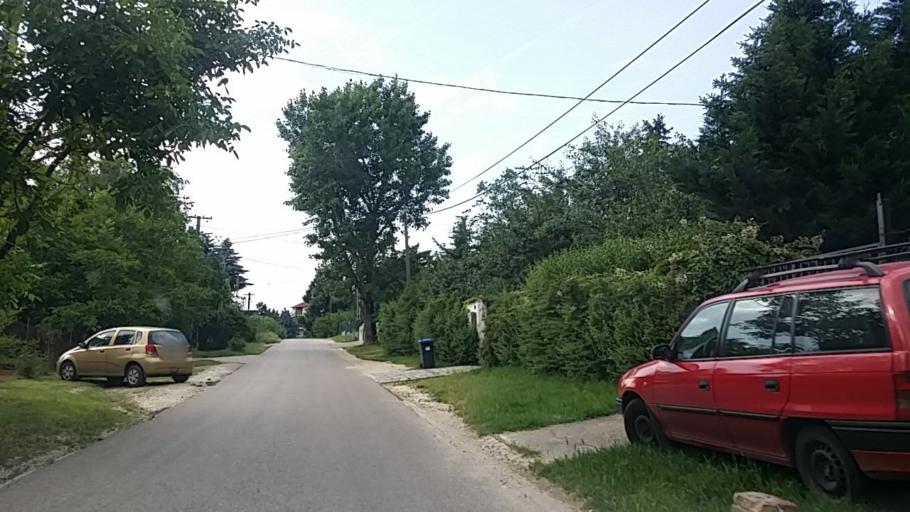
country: HU
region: Pest
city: Erd
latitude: 47.3950
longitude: 18.9277
